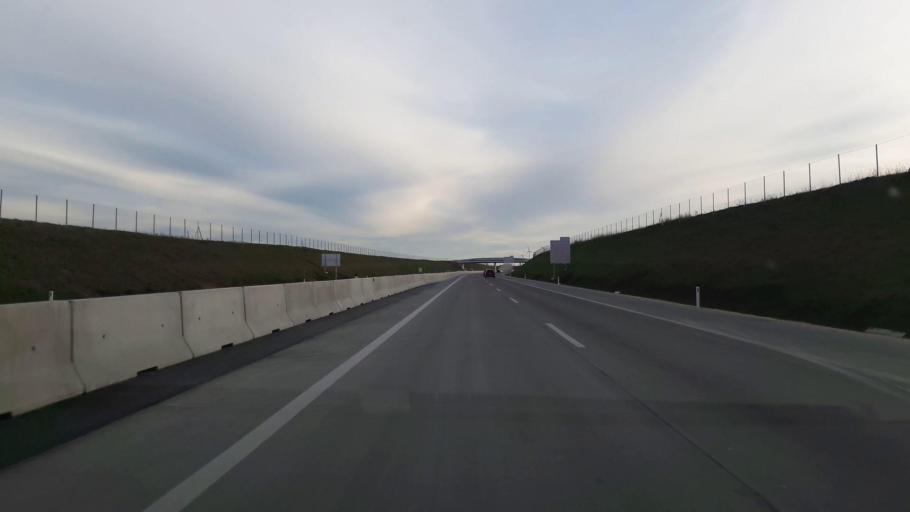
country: AT
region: Lower Austria
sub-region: Politischer Bezirk Mistelbach
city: Wilfersdorf
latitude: 48.5702
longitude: 16.6294
